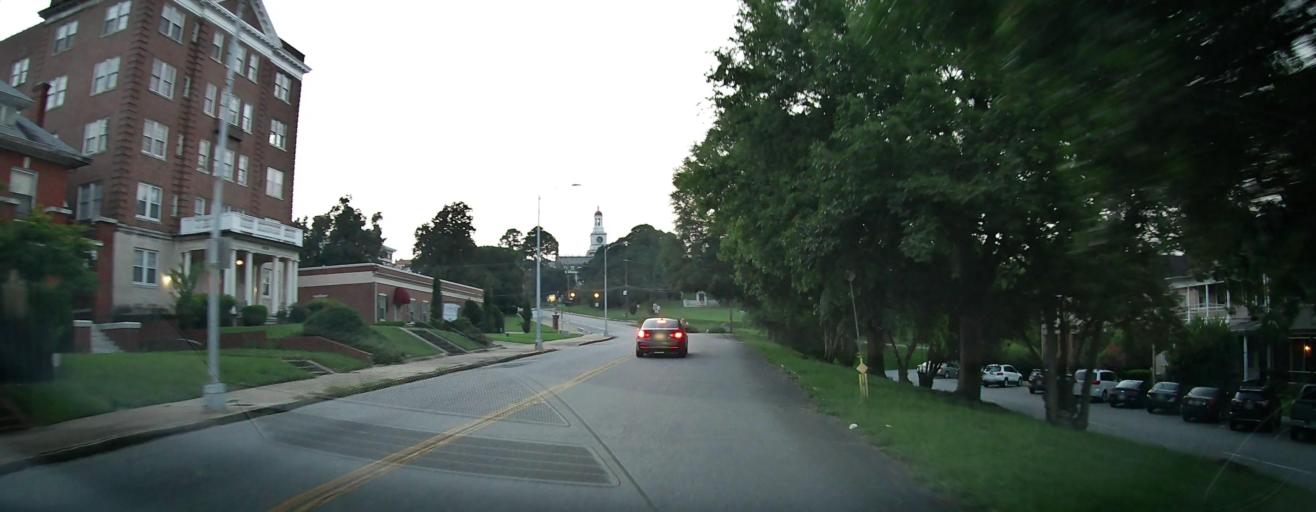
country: US
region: Georgia
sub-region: Bibb County
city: Macon
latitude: 32.8402
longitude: -83.6317
